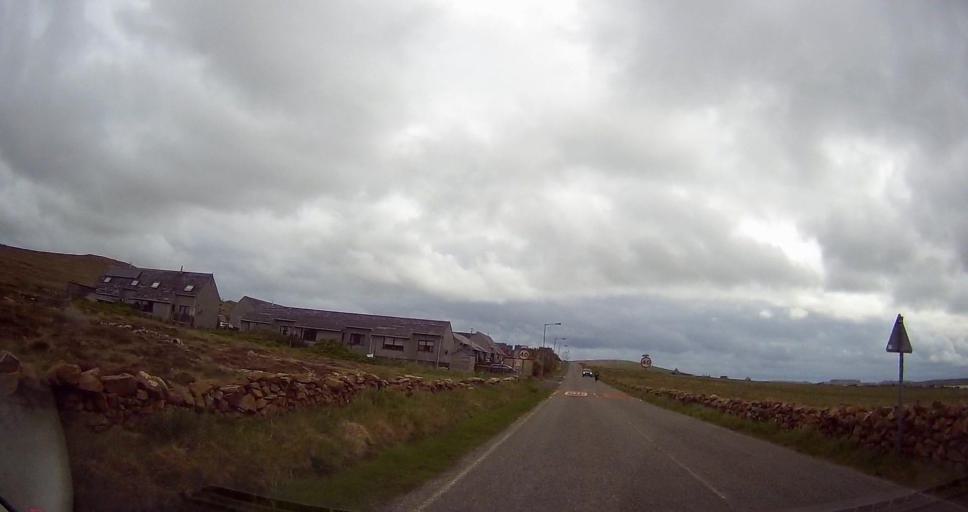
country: GB
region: Scotland
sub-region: Shetland Islands
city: Shetland
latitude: 60.7616
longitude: -0.8723
